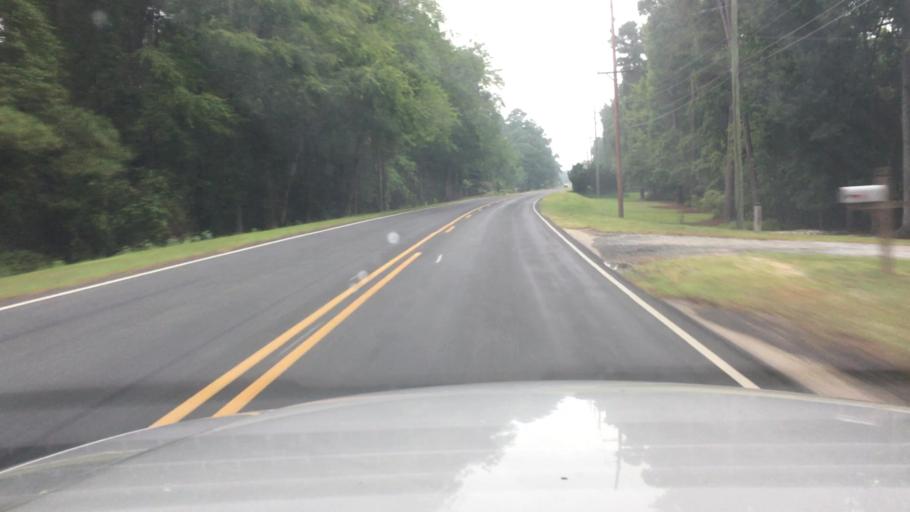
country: US
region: North Carolina
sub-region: Cumberland County
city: Fayetteville
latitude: 35.0008
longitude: -78.8582
